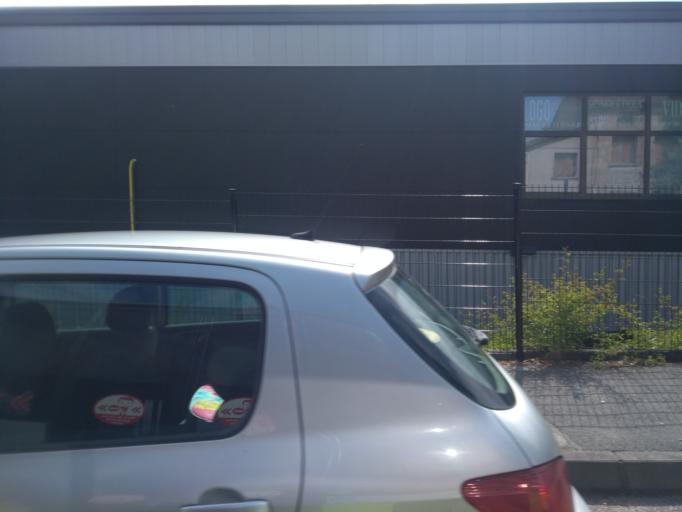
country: FR
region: Rhone-Alpes
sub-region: Departement de la Loire
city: Saint-Genest-Lerpt
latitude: 45.4409
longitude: 4.3409
